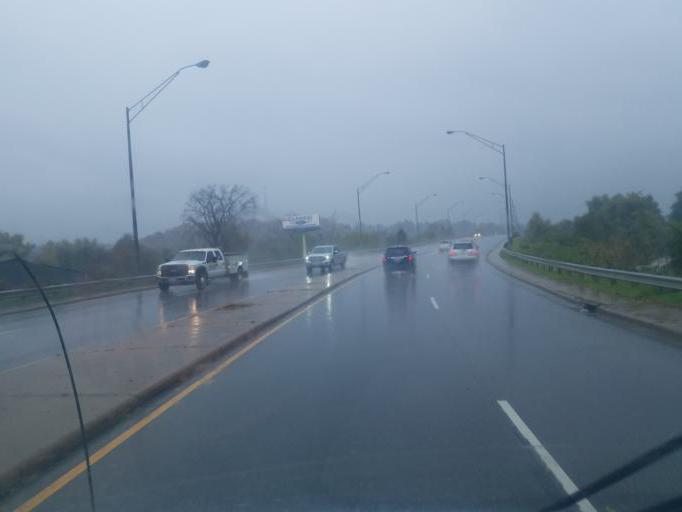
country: US
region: Ohio
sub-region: Muskingum County
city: Zanesville
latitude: 39.9522
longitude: -82.0035
